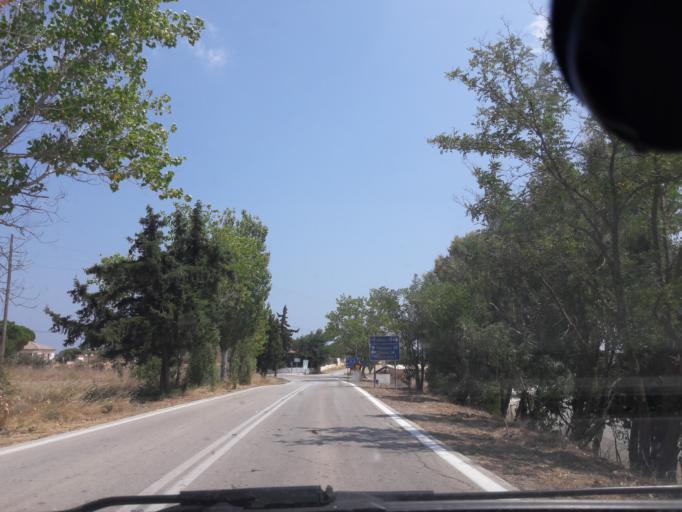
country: GR
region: North Aegean
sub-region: Nomos Lesvou
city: Myrina
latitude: 39.9238
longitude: 25.3292
